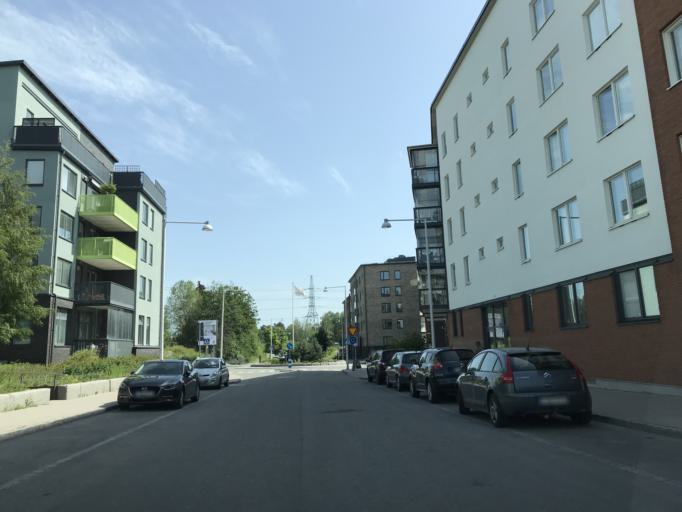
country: SE
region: Stockholm
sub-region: Solna Kommun
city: Rasunda
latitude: 59.3838
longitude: 17.9849
